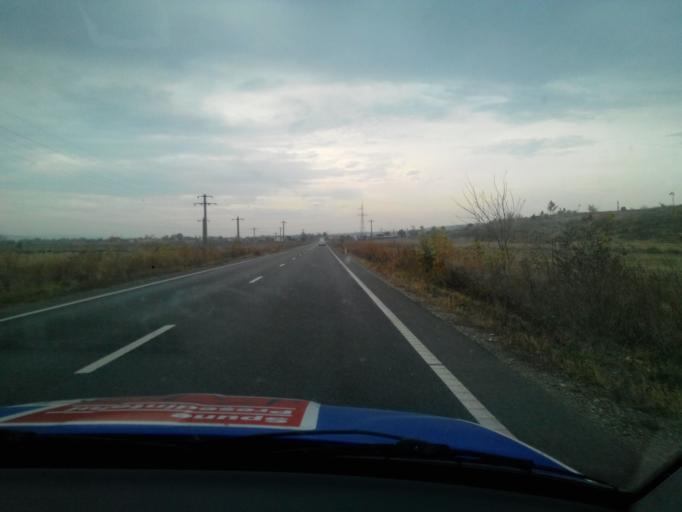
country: RO
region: Vaslui
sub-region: Comuna Zorleni
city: Zorleni
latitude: 46.2775
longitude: 27.7058
